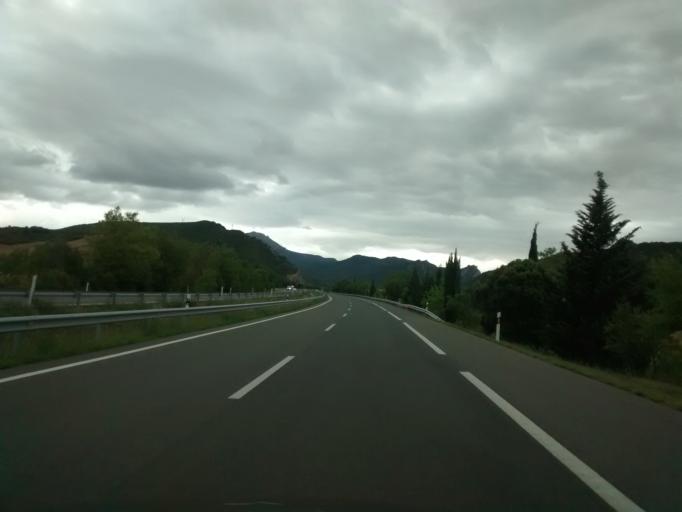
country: ES
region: Basque Country
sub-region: Provincia de Alava
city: Zambrana
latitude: 42.6435
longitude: -2.8726
